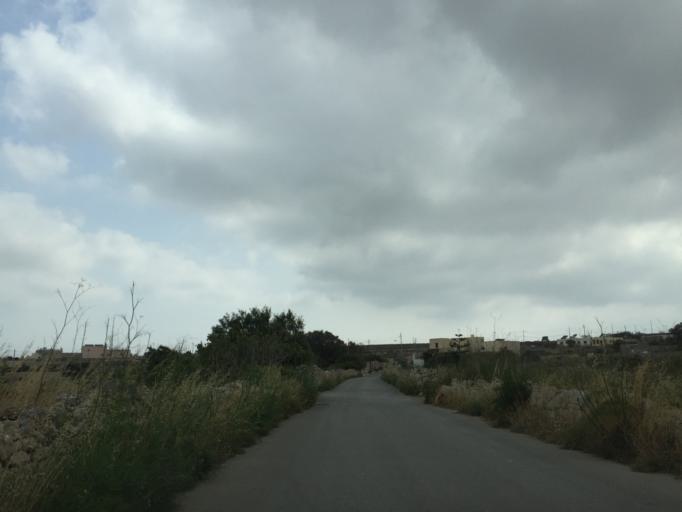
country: MT
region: L-Imtarfa
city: Imtarfa
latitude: 35.9020
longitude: 14.3802
